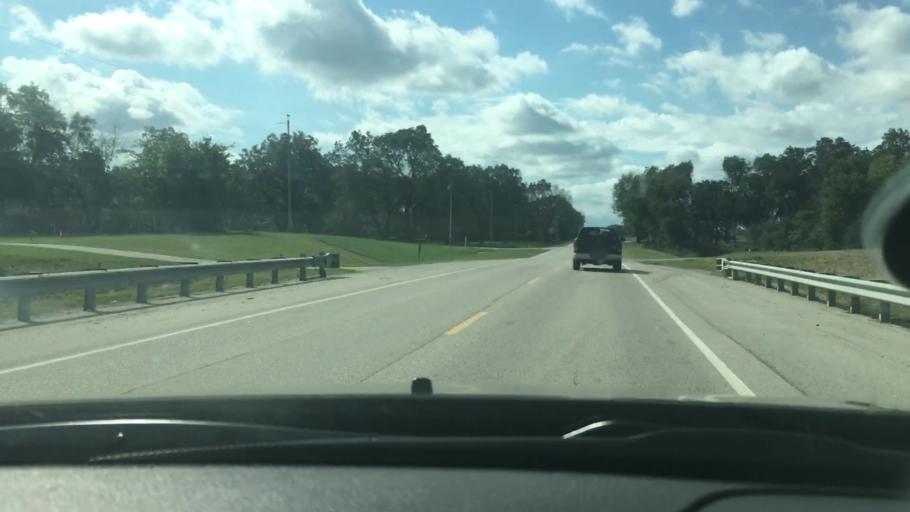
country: US
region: Oklahoma
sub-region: Pontotoc County
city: Ada
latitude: 34.7025
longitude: -96.6349
